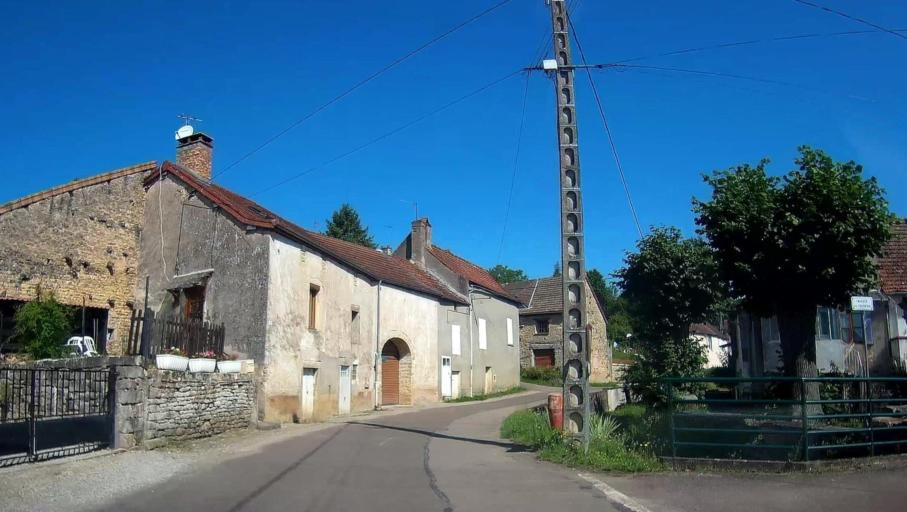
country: FR
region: Bourgogne
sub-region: Departement de la Cote-d'Or
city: Nolay
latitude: 46.9673
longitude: 4.6429
